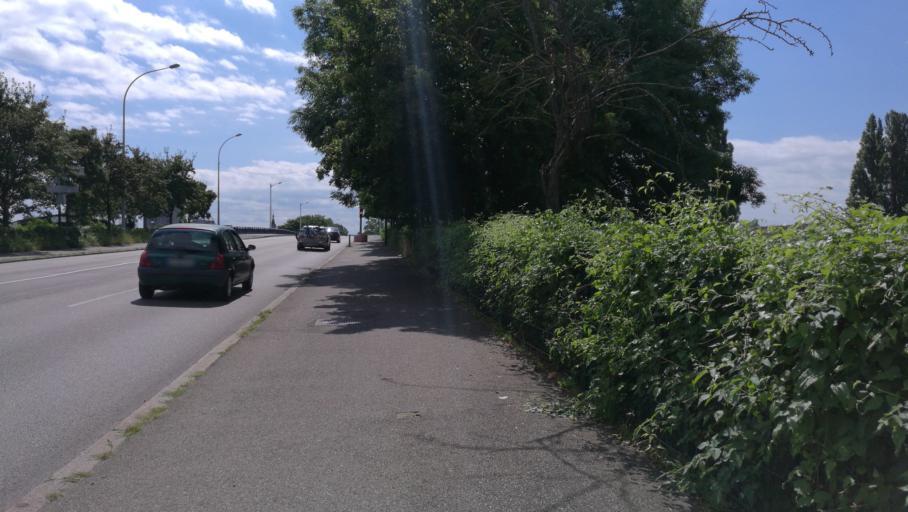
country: FR
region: Alsace
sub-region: Departement du Bas-Rhin
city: Strasbourg
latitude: 48.5801
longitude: 7.7801
